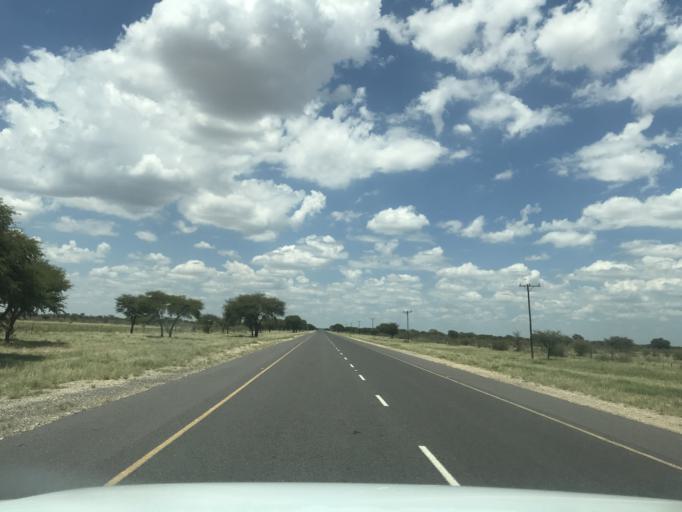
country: BW
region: South East
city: Janeng
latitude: -25.6971
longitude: 25.1265
